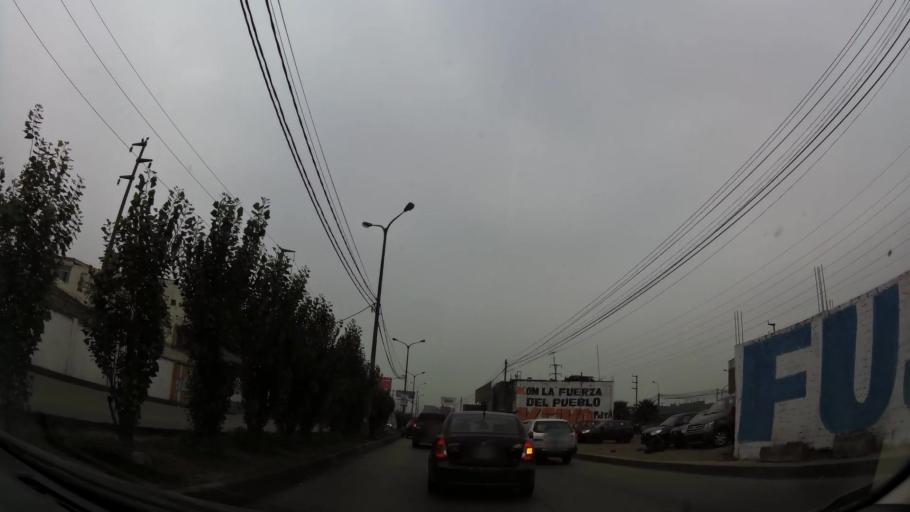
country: PE
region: Lima
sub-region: Lima
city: Santa Maria
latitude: -12.0219
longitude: -76.9075
